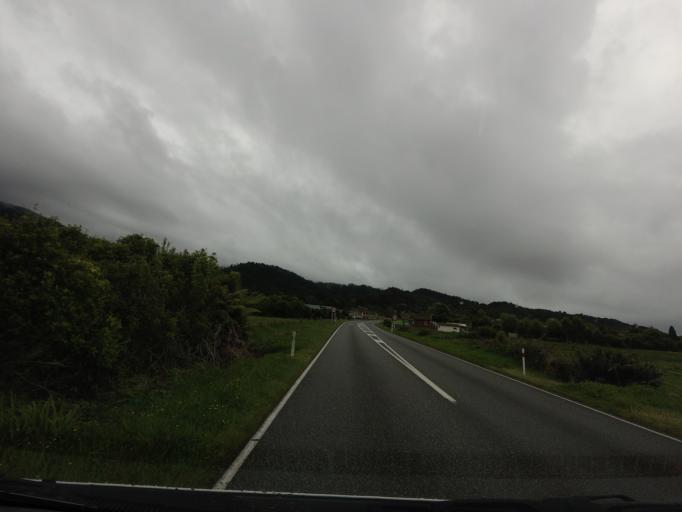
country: NZ
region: West Coast
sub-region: Westland District
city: Hokitika
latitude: -42.8973
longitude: 170.8212
